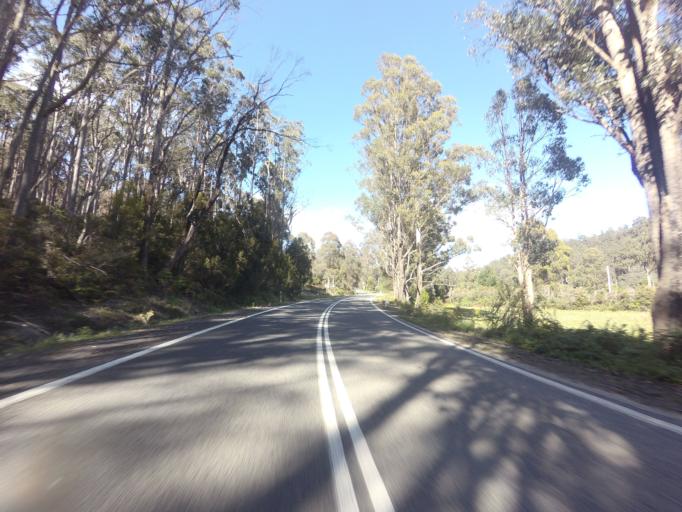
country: AU
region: Tasmania
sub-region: Derwent Valley
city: New Norfolk
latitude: -42.7049
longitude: 146.7128
